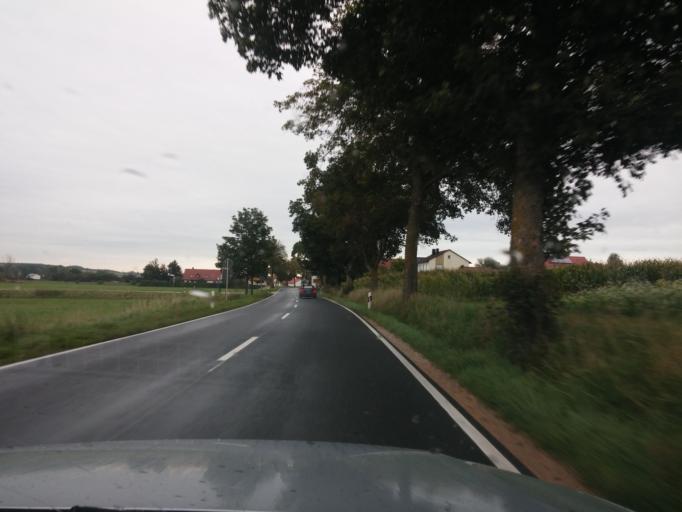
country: DE
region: Bavaria
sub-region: Upper Bavaria
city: Hohenkammer
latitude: 48.4269
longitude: 11.5470
